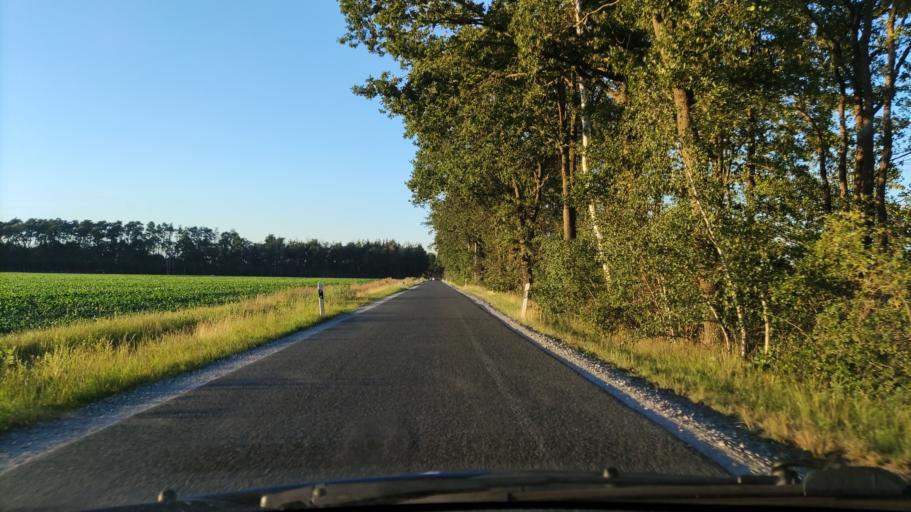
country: DE
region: Lower Saxony
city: Klein Gusborn
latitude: 53.0643
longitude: 11.1862
